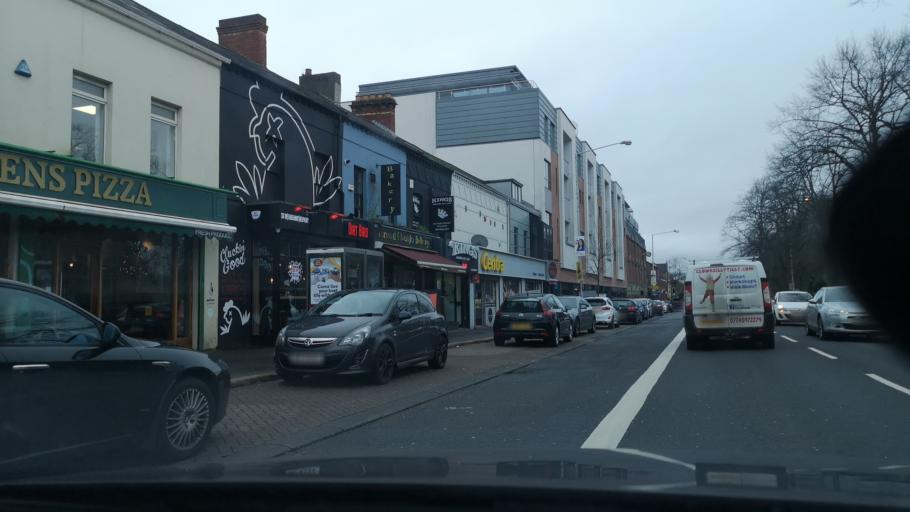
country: GB
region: Northern Ireland
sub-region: City of Belfast
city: Belfast
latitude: 54.5786
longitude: -5.9193
